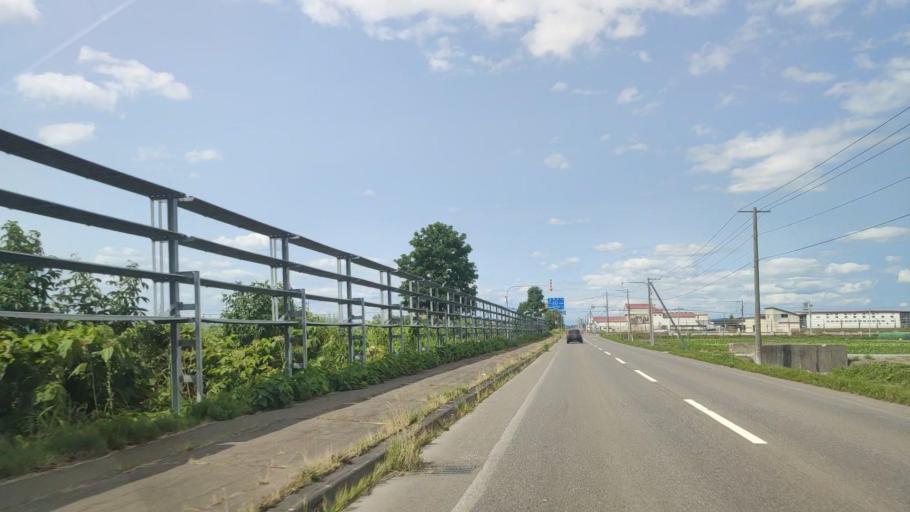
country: JP
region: Hokkaido
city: Nayoro
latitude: 44.1992
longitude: 142.4158
